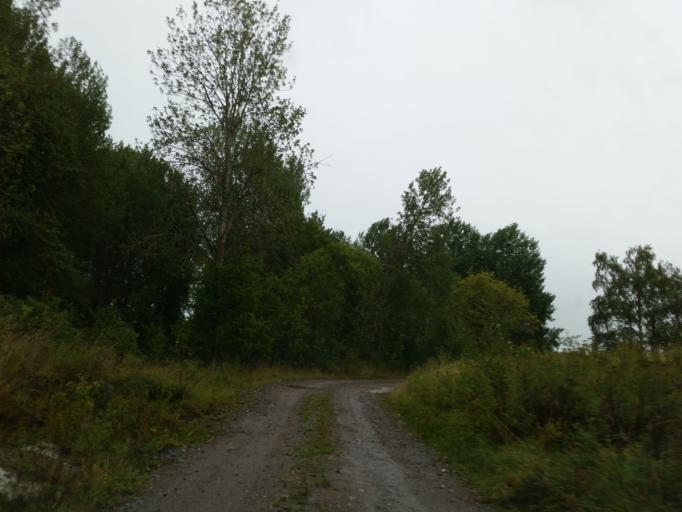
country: SE
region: Uppsala
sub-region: Habo Kommun
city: Balsta
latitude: 59.6451
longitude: 17.4815
